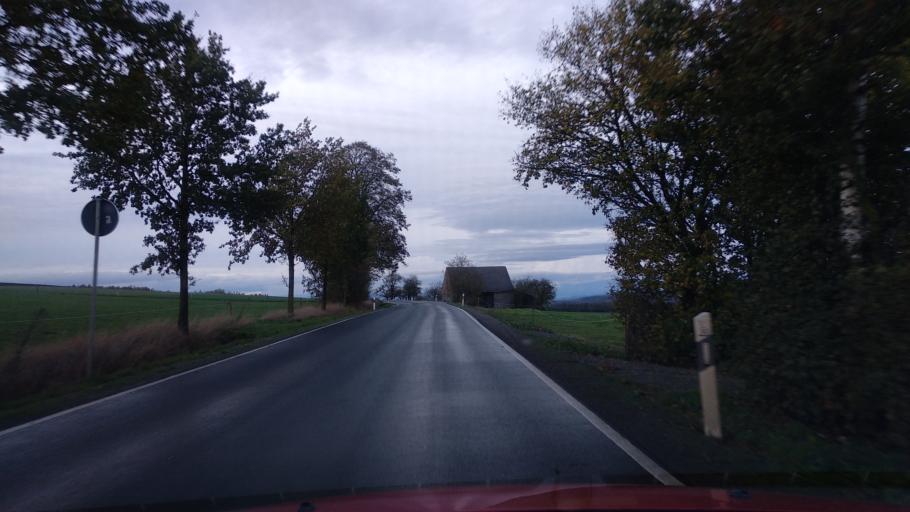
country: DE
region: North Rhine-Westphalia
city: Borgentreich
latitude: 51.6610
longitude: 9.2690
